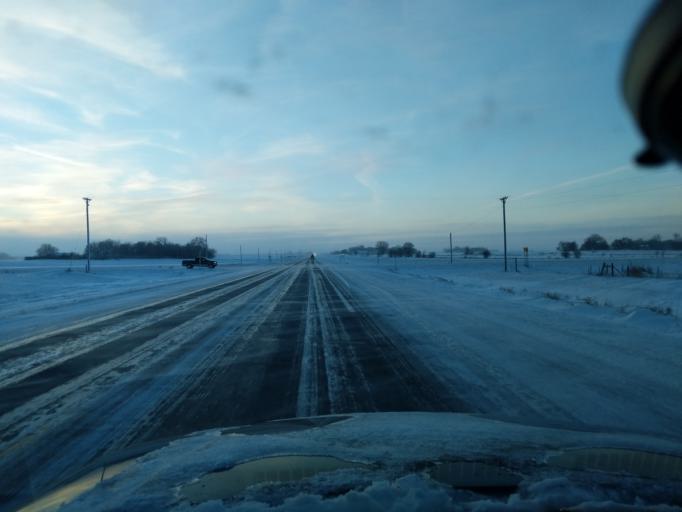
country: US
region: Minnesota
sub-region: Renville County
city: Renville
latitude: 44.7891
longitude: -95.2991
